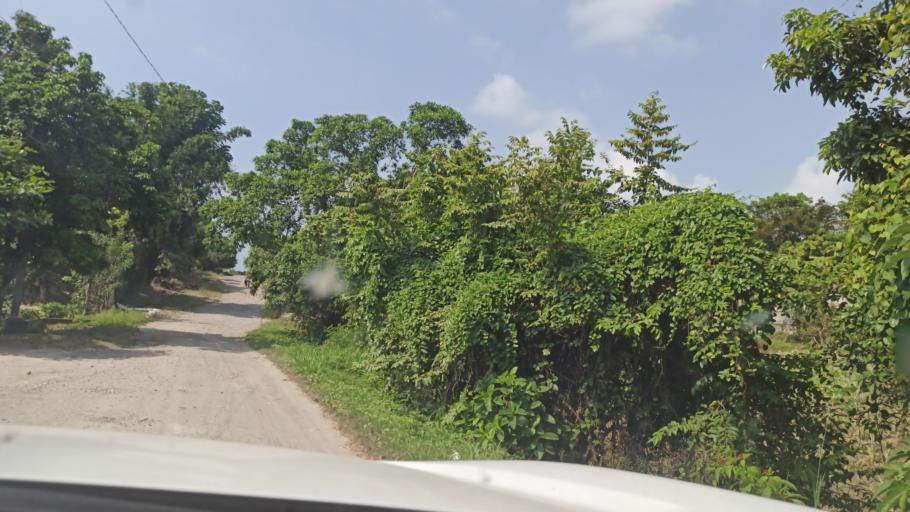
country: MX
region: Veracruz
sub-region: Martinez de la Torre
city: El Progreso
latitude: 20.1472
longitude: -97.0663
